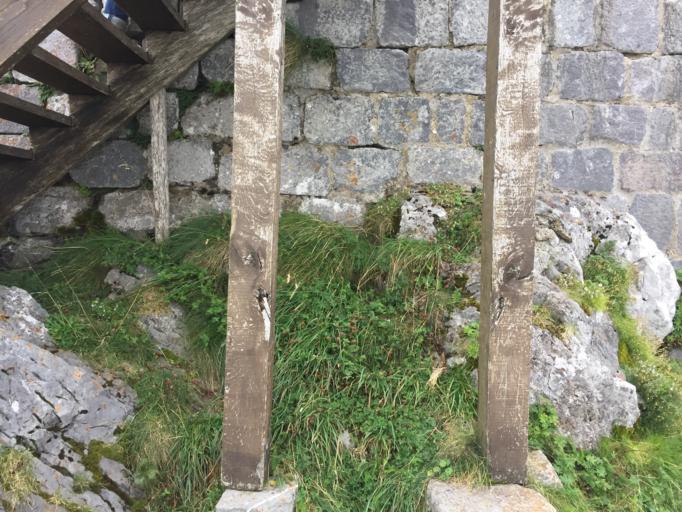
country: FR
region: Midi-Pyrenees
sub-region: Departement de l'Ariege
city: Lavelanet
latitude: 42.8759
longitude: 1.8322
